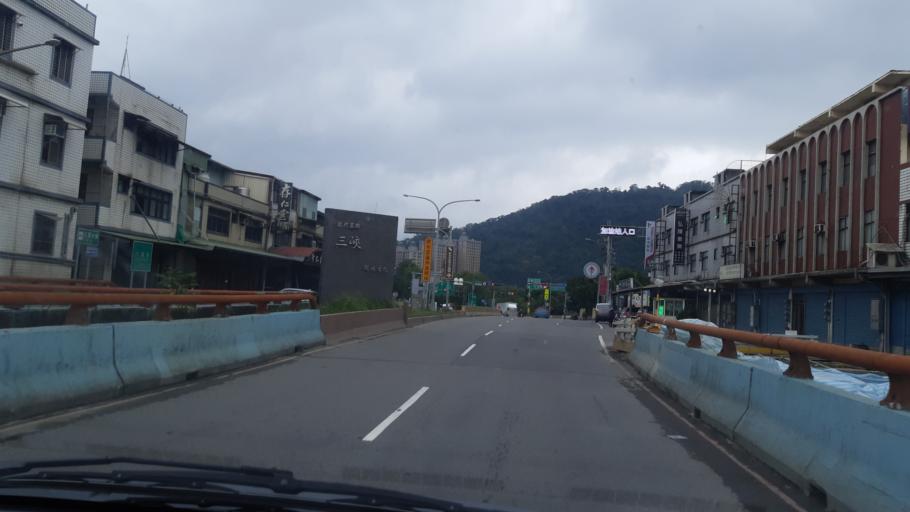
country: TW
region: Taiwan
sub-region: Taoyuan
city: Taoyuan
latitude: 24.9416
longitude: 121.3557
